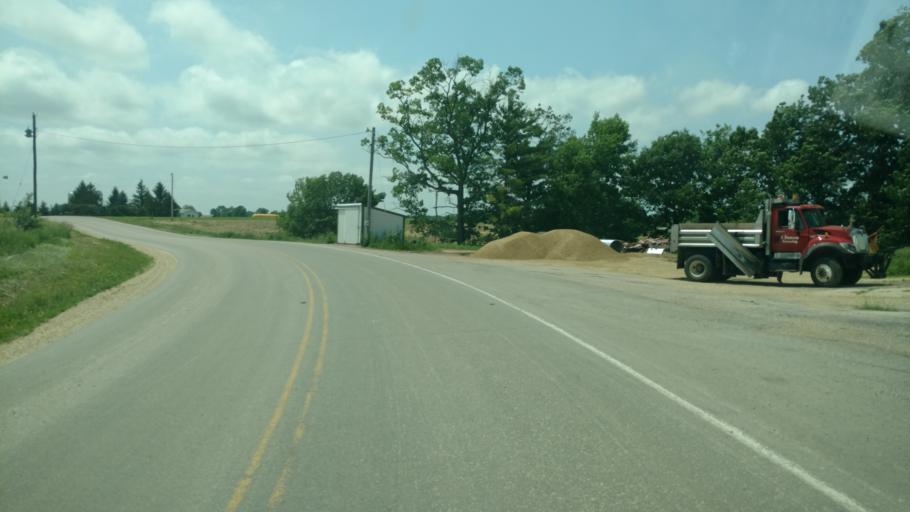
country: US
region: Wisconsin
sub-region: Monroe County
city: Cashton
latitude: 43.6966
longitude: -90.7295
